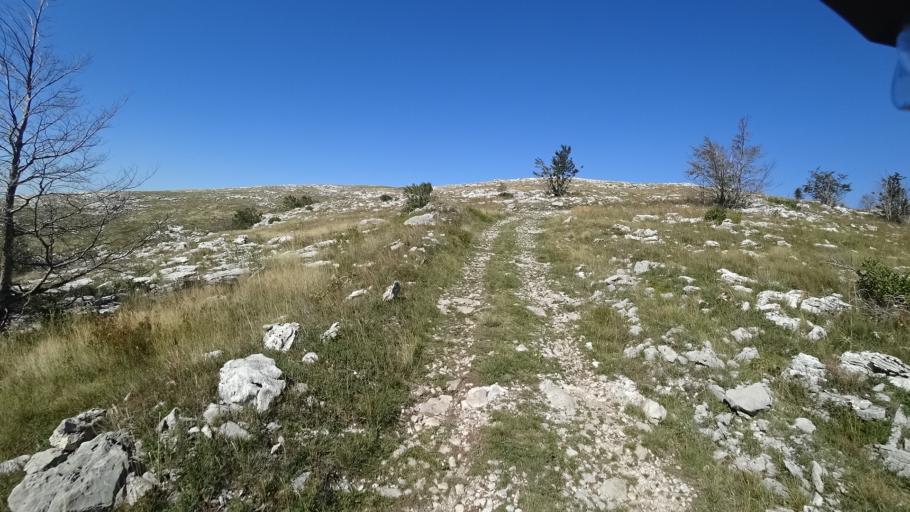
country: HR
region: Splitsko-Dalmatinska
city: Hrvace
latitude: 43.9113
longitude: 16.6110
